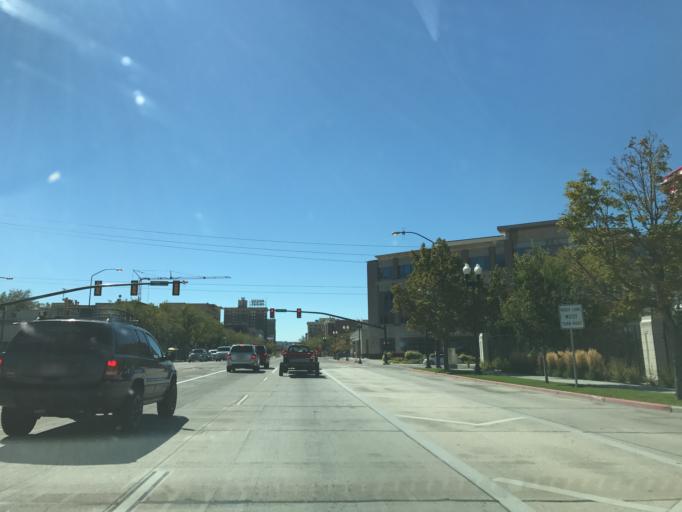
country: US
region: Utah
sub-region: Weber County
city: Ogden
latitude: 41.2276
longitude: -111.9705
